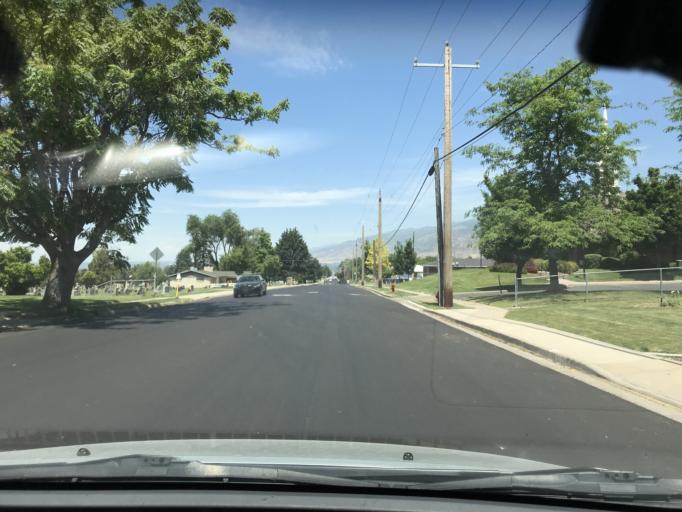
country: US
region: Utah
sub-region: Davis County
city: Woods Cross
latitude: 40.8648
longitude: -111.8857
